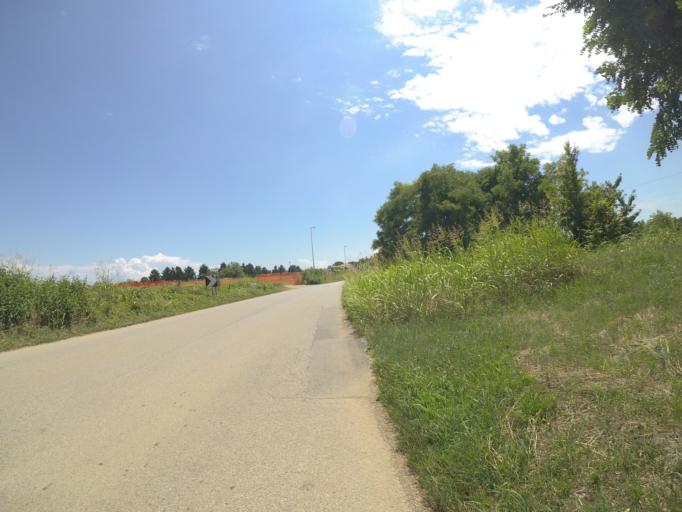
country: IT
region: Friuli Venezia Giulia
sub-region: Provincia di Udine
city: Lestizza
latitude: 45.9748
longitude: 13.1564
